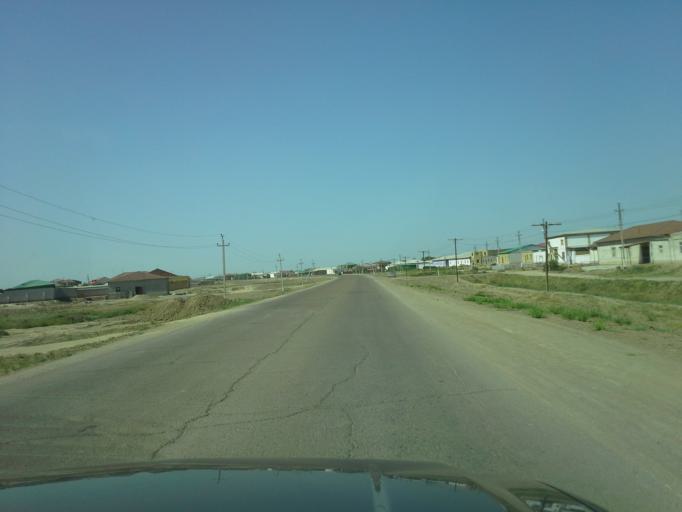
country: TM
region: Dasoguz
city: Dasoguz
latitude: 41.8026
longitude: 60.0135
